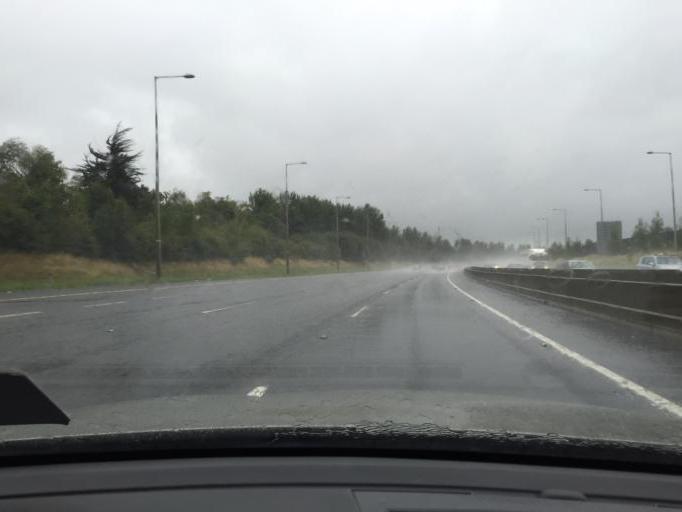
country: IE
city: Cherry Orchard
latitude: 53.3371
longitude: -6.3865
